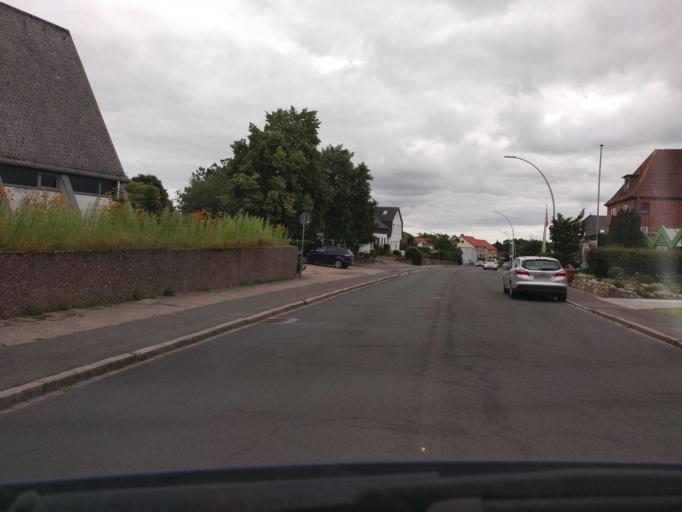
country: DE
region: Schleswig-Holstein
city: Schleswig
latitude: 54.5243
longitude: 9.5378
